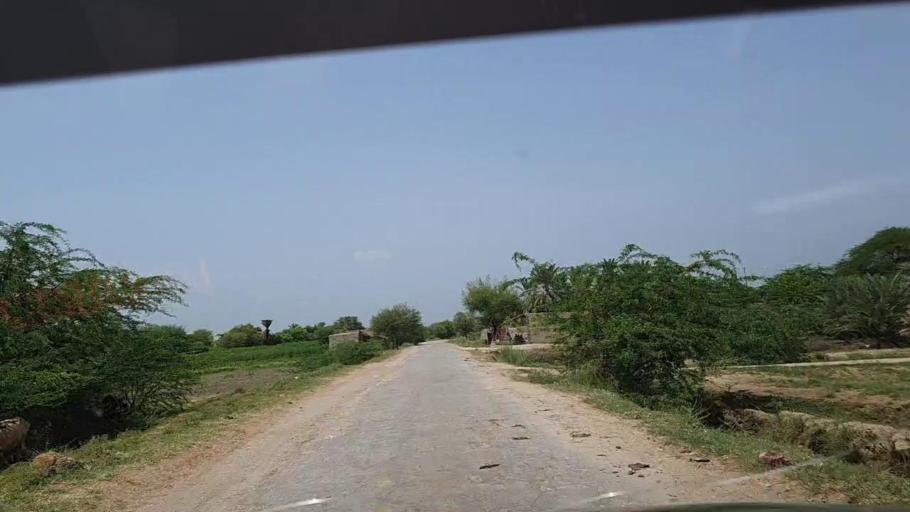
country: PK
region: Sindh
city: Khanpur
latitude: 27.7989
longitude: 69.4520
